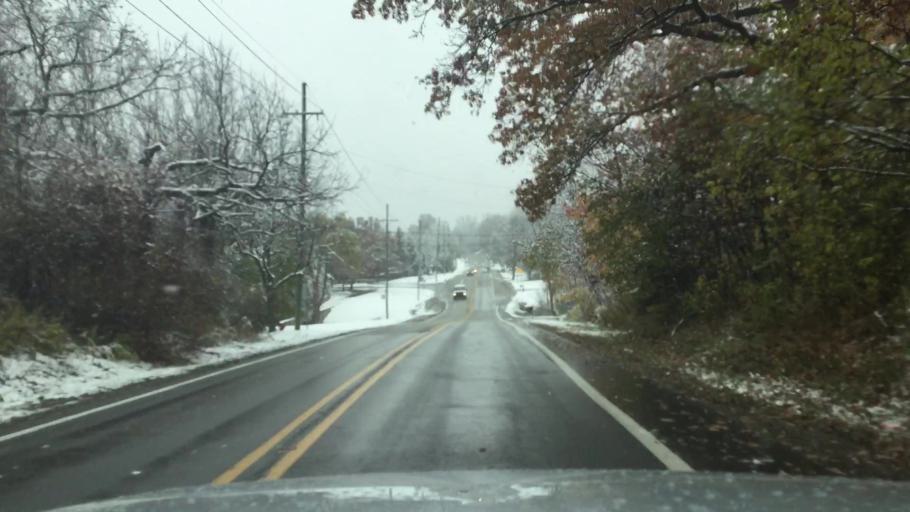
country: US
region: Michigan
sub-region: Oakland County
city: Orchard Lake
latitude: 42.5612
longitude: -83.3416
